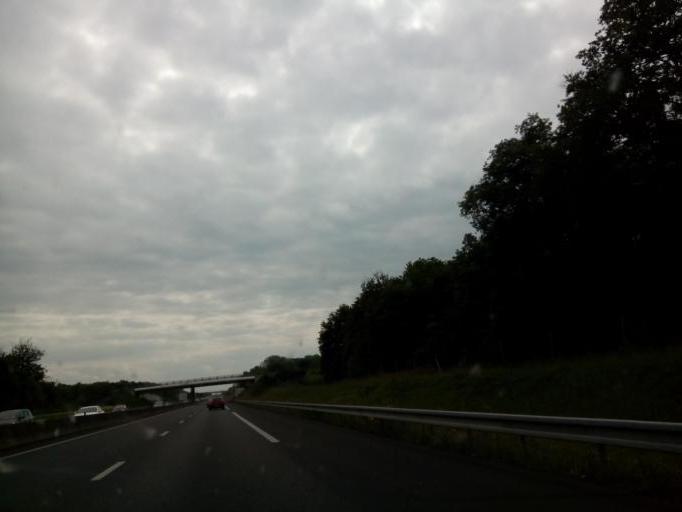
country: FR
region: Pays de la Loire
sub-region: Departement de Maine-et-Loire
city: Saint-Lambert-la-Potherie
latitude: 47.4756
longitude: -0.6750
